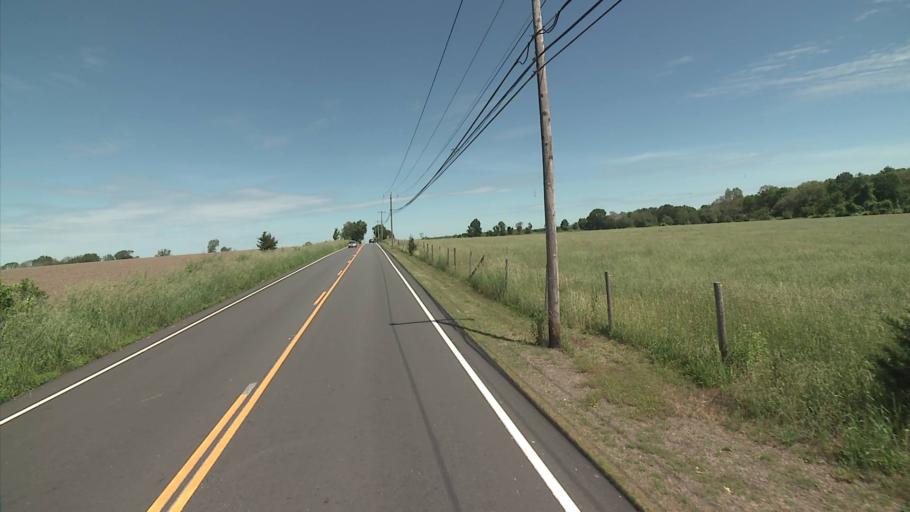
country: US
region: Connecticut
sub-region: Windham County
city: Moosup
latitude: 41.6677
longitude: -71.8476
